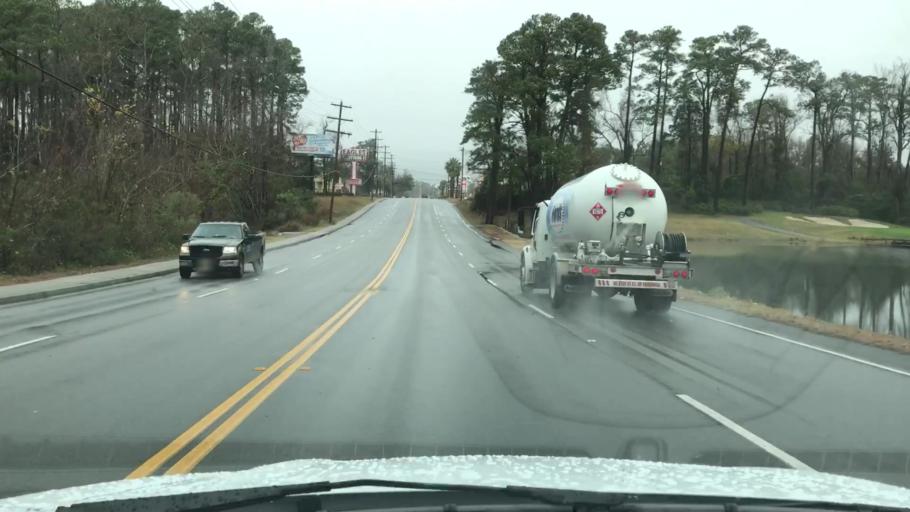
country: US
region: South Carolina
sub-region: Horry County
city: North Myrtle Beach
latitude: 33.7731
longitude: -78.7896
